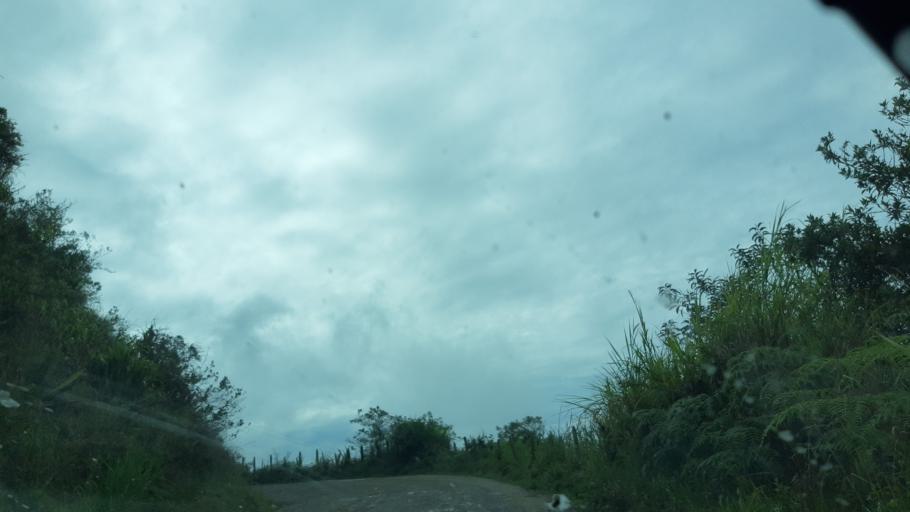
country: CO
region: Boyaca
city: Guateque
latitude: 5.0334
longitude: -73.4422
